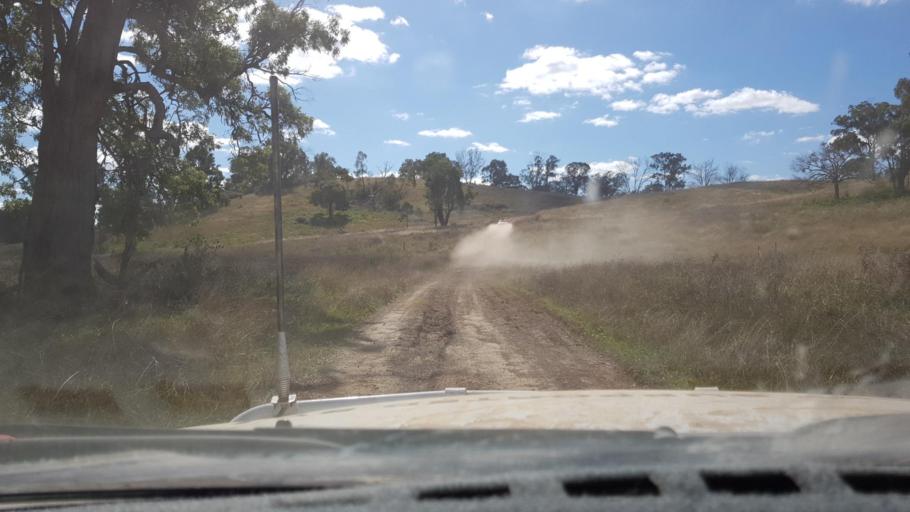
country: AU
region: New South Wales
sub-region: Tamworth Municipality
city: Manilla
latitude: -30.4405
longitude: 150.8380
